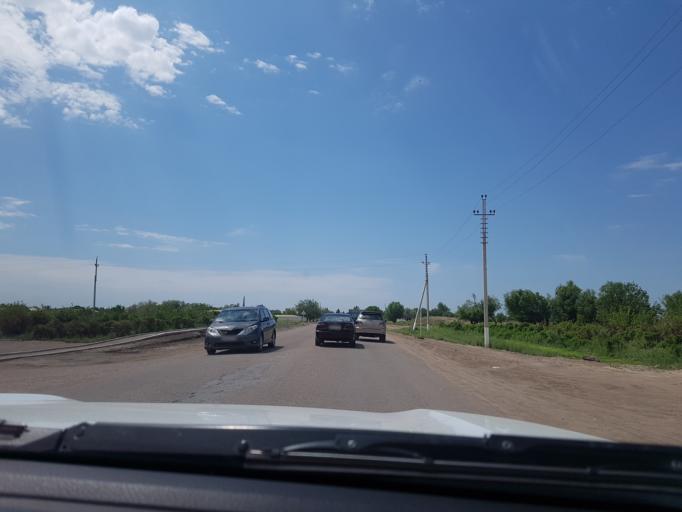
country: TM
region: Dasoguz
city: Koeneuergench
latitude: 42.3228
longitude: 59.1402
